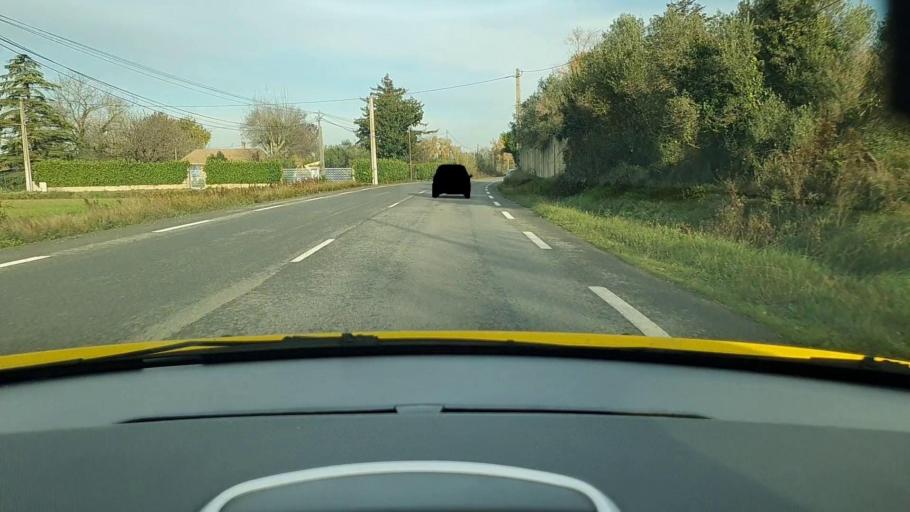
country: FR
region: Languedoc-Roussillon
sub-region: Departement du Gard
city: Fourques
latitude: 43.7120
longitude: 4.6066
